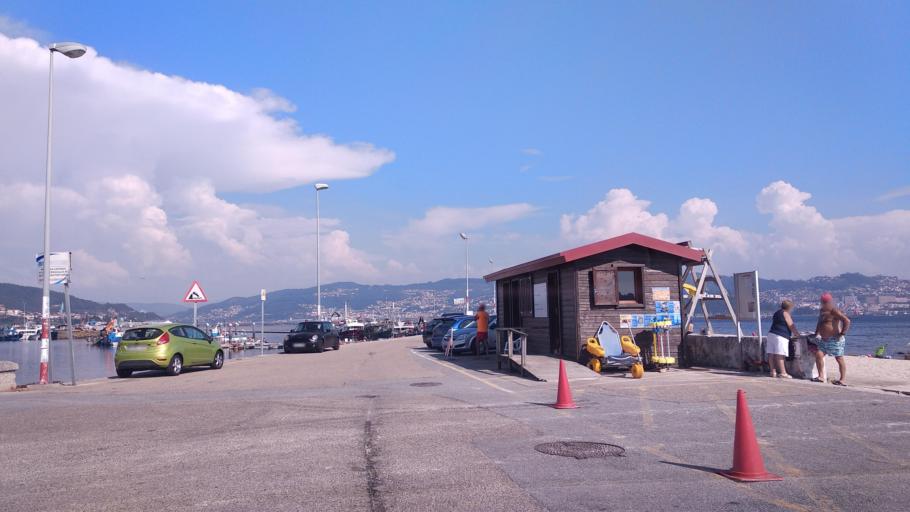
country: ES
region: Galicia
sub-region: Provincia de Pontevedra
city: Moana
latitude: 42.2711
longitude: -8.7403
